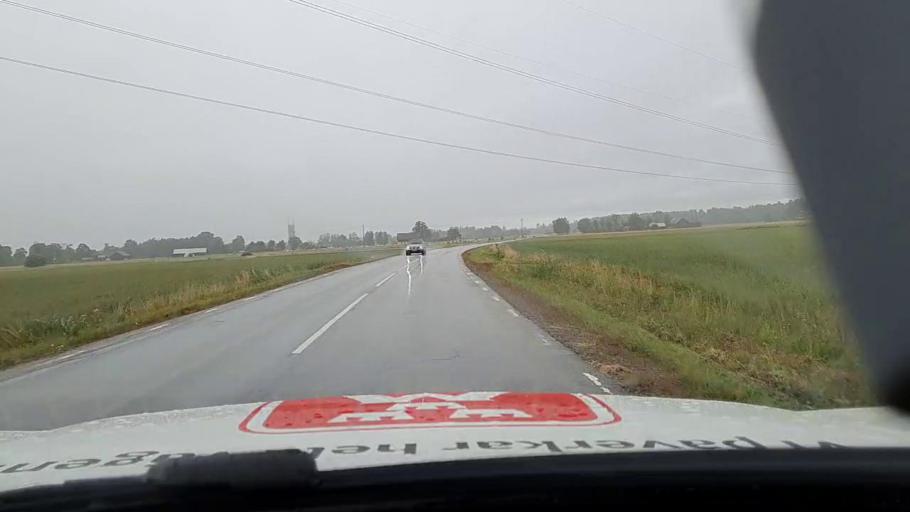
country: SE
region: Vaestra Goetaland
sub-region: Toreboda Kommun
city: Toereboda
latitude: 58.6900
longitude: 14.1277
